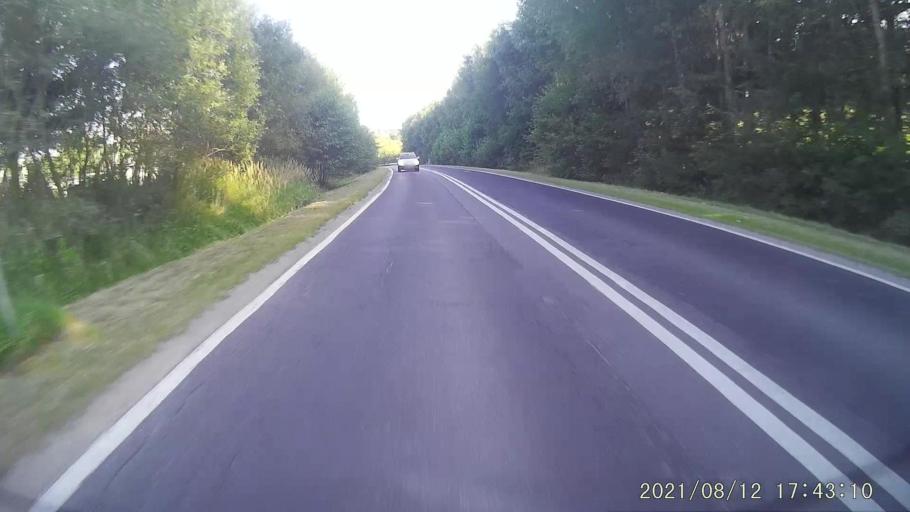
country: PL
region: Lower Silesian Voivodeship
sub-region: Powiat klodzki
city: Ladek-Zdroj
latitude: 50.3405
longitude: 16.8026
